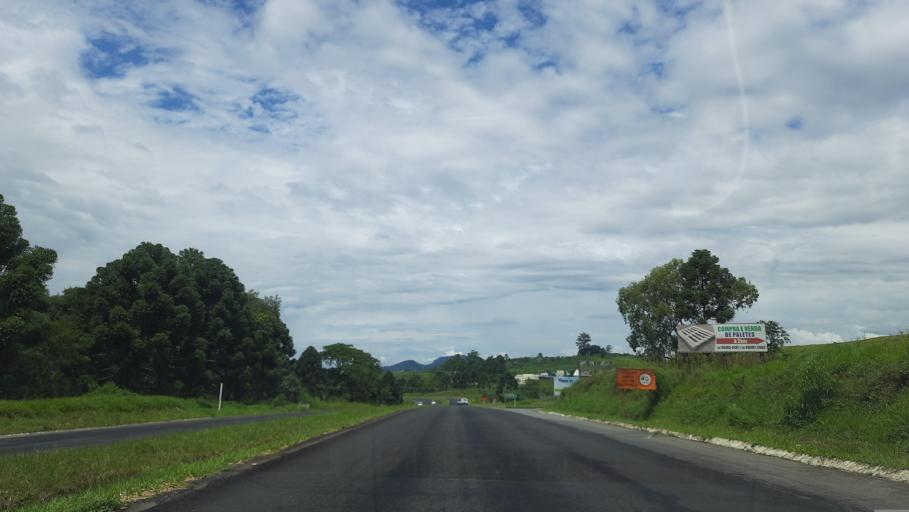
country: BR
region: Minas Gerais
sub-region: Pocos De Caldas
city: Pocos de Caldas
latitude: -21.8234
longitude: -46.6691
